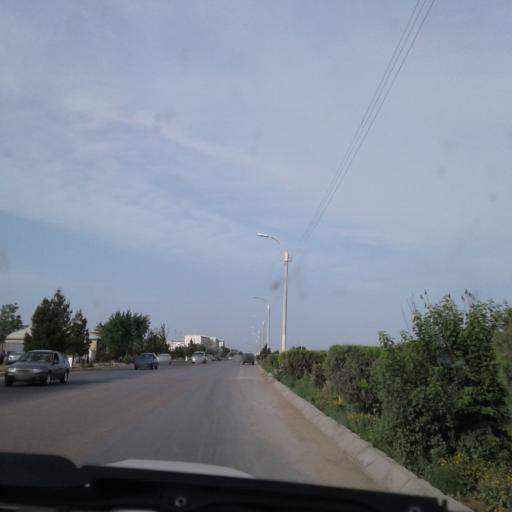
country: TM
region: Mary
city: Mary
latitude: 37.5788
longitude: 61.8692
